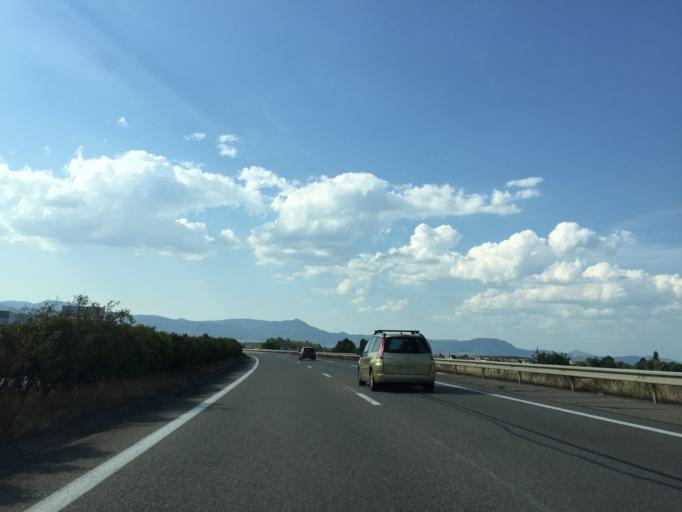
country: FR
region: Alsace
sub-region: Departement du Haut-Rhin
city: Houssen
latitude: 48.1133
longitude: 7.3813
